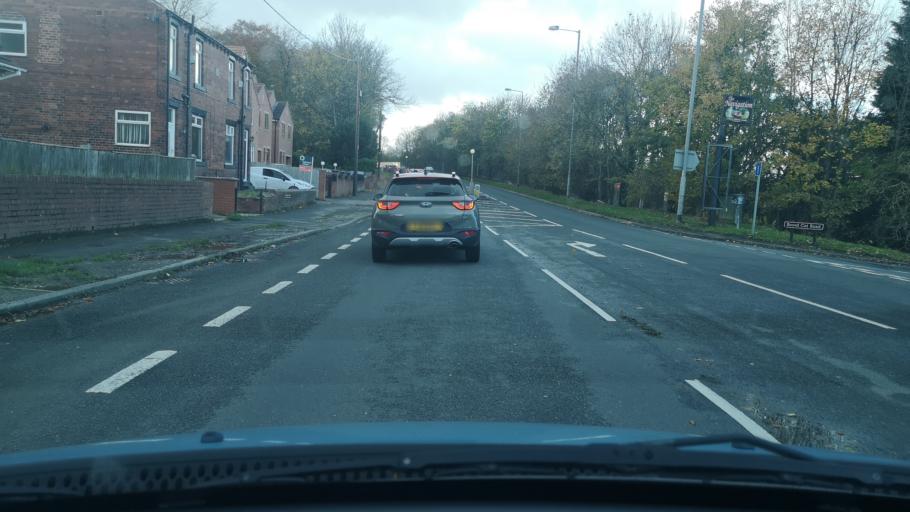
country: GB
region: England
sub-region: City and Borough of Wakefield
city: Crigglestone
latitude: 53.6471
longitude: -1.5401
